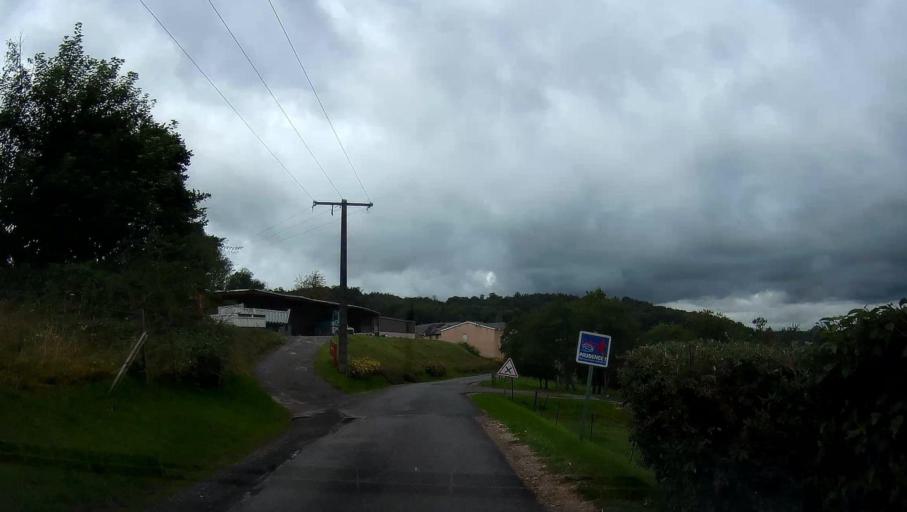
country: FR
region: Champagne-Ardenne
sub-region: Departement des Ardennes
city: Rimogne
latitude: 49.7698
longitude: 4.4771
